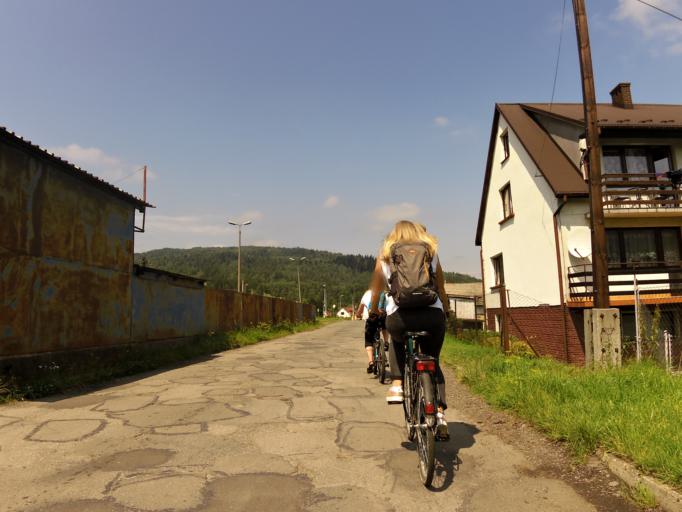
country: PL
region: Silesian Voivodeship
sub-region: Powiat zywiecki
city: Rajcza
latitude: 49.5185
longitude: 19.1113
